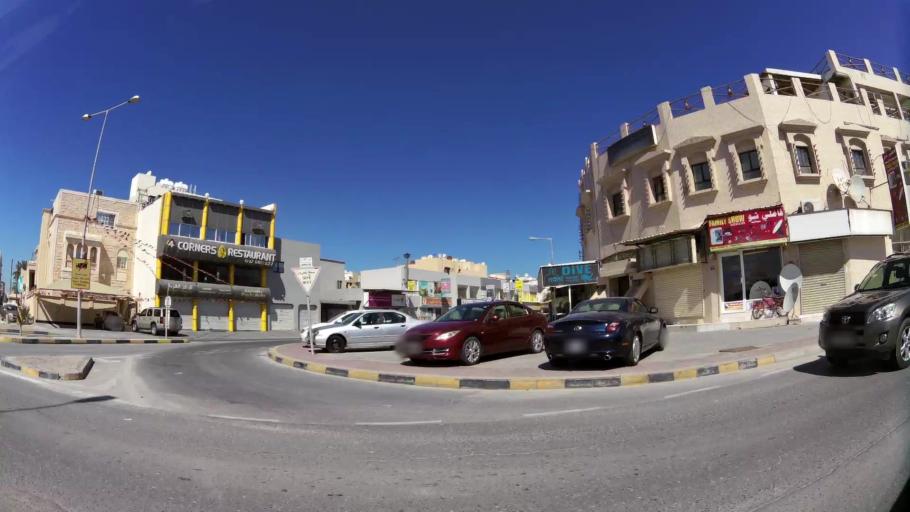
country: BH
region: Muharraq
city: Al Hadd
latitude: 26.2681
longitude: 50.6532
